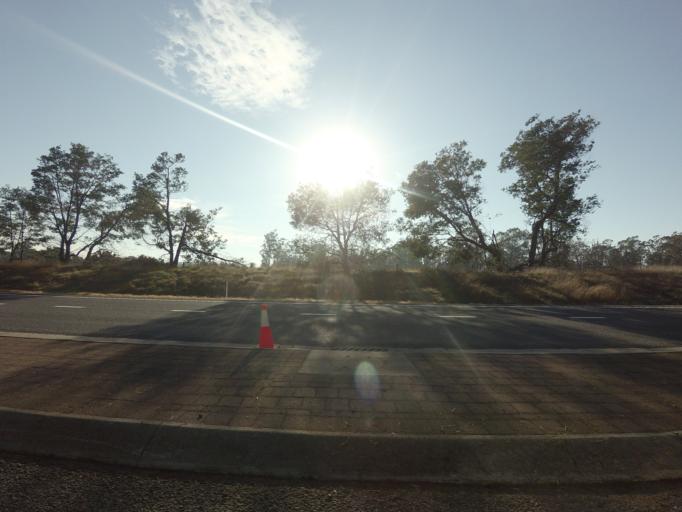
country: AU
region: Tasmania
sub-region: Northern Midlands
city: Longford
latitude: -41.5371
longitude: 147.0483
